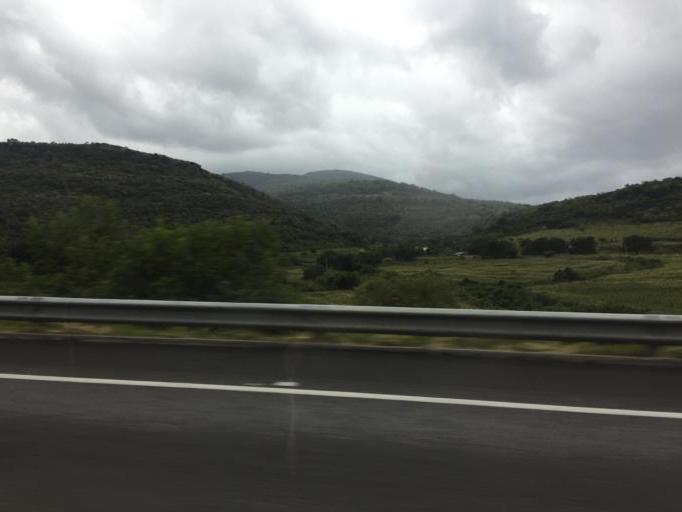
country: MX
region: Jalisco
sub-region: Zapotlanejo
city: La Mezquitera
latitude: 20.5369
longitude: -103.0186
